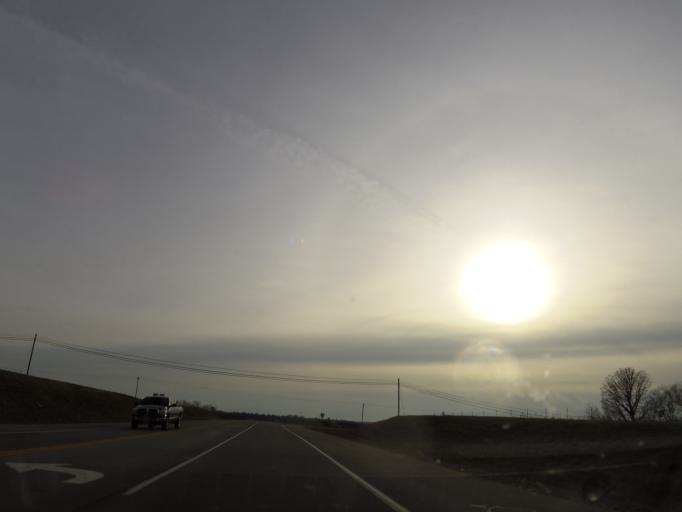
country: US
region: Kentucky
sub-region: Harrison County
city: Cynthiana
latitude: 38.3945
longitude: -84.3203
